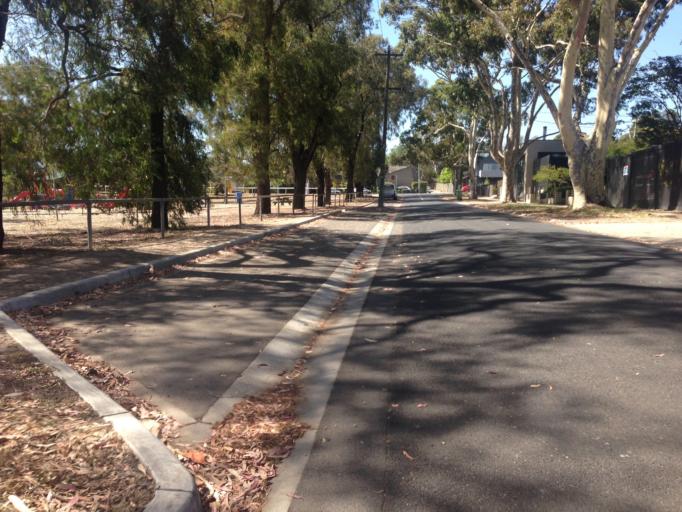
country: AU
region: Victoria
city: Ivanhoe East
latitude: -37.7731
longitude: 145.0531
